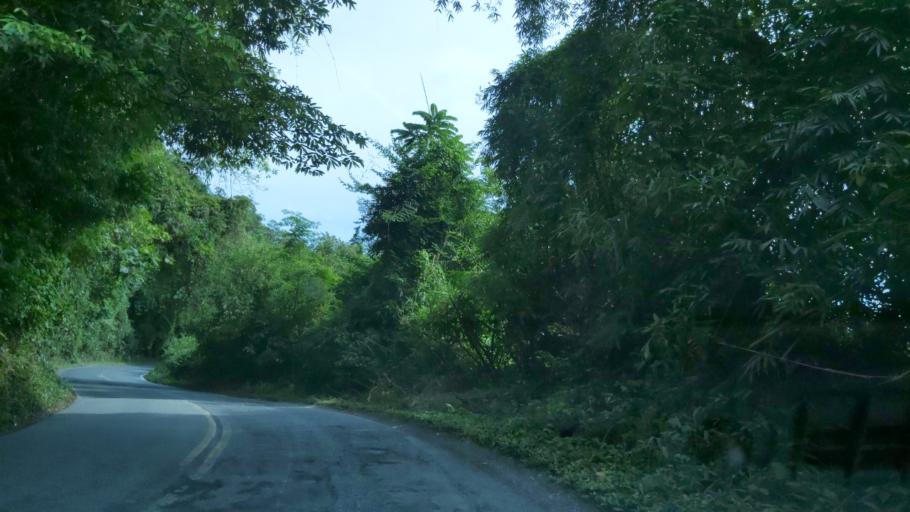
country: BR
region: Sao Paulo
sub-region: Juquia
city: Juquia
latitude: -24.0928
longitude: -47.6159
